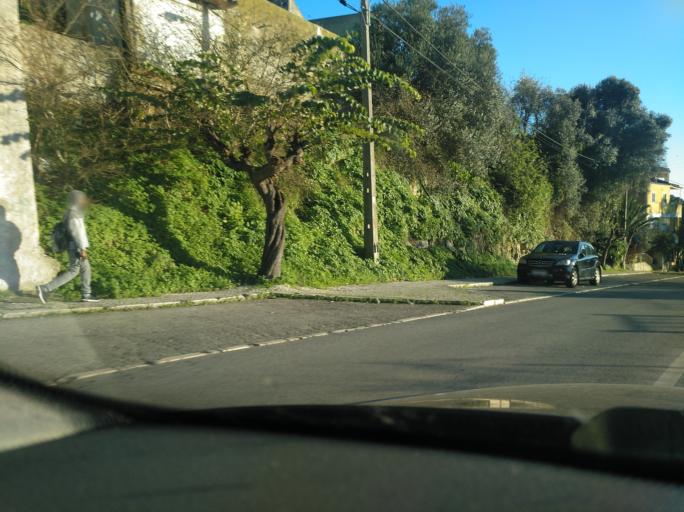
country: PT
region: Lisbon
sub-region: Loures
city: Camarate
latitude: 38.8124
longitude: -9.1189
